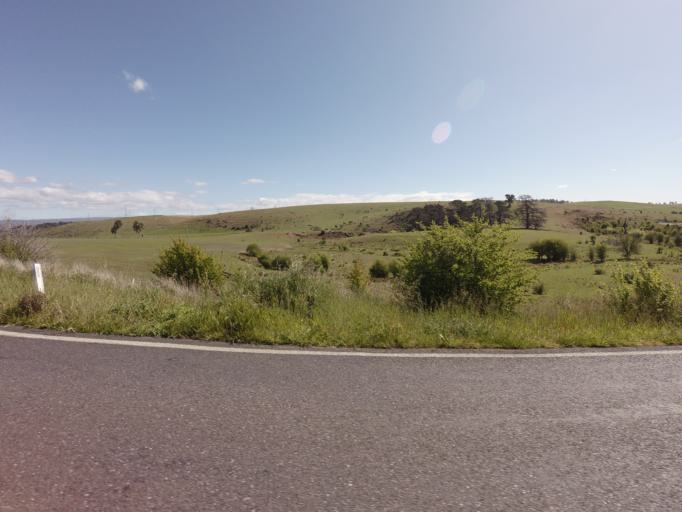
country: AU
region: Tasmania
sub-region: Derwent Valley
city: New Norfolk
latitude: -42.6535
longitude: 146.9358
